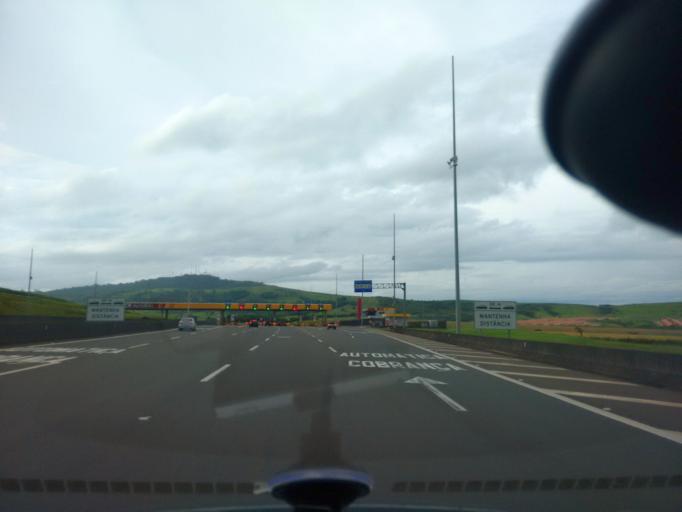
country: BR
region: Sao Paulo
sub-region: Limeira
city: Limeira
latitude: -22.5577
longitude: -47.4598
